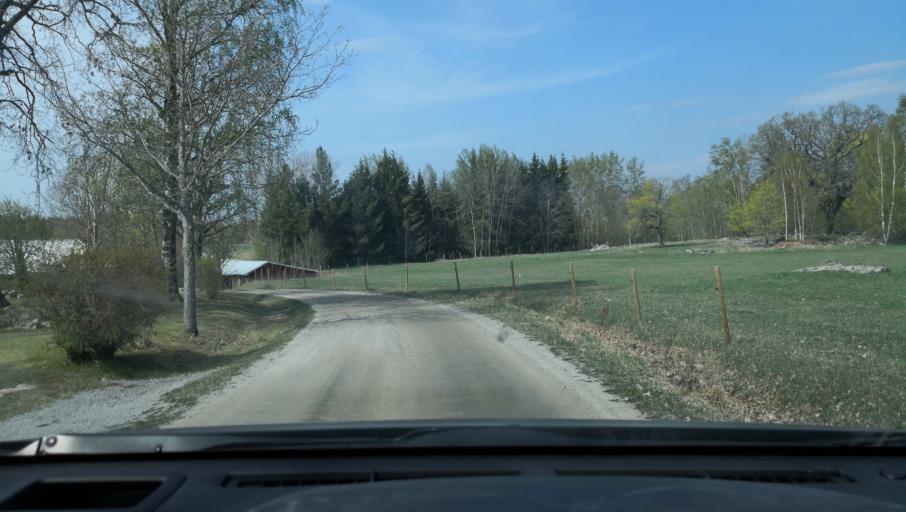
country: SE
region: Vaestmanland
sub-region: Vasteras
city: Skultuna
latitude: 59.7687
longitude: 16.4495
